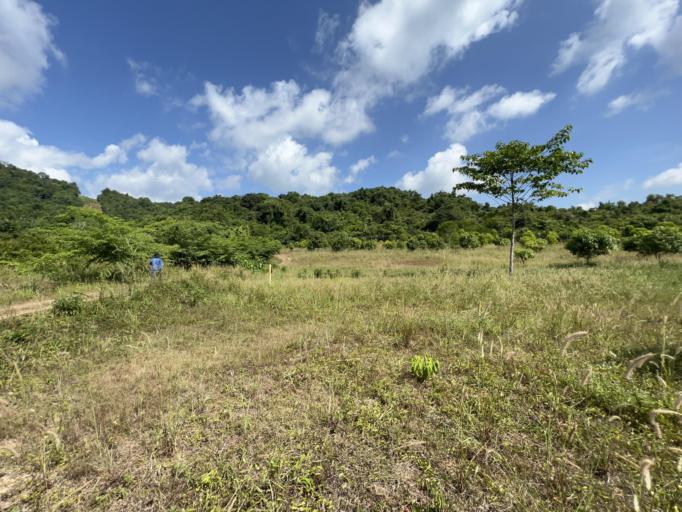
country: MM
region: Tanintharyi
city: Dawei
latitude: 14.6039
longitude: 97.9736
